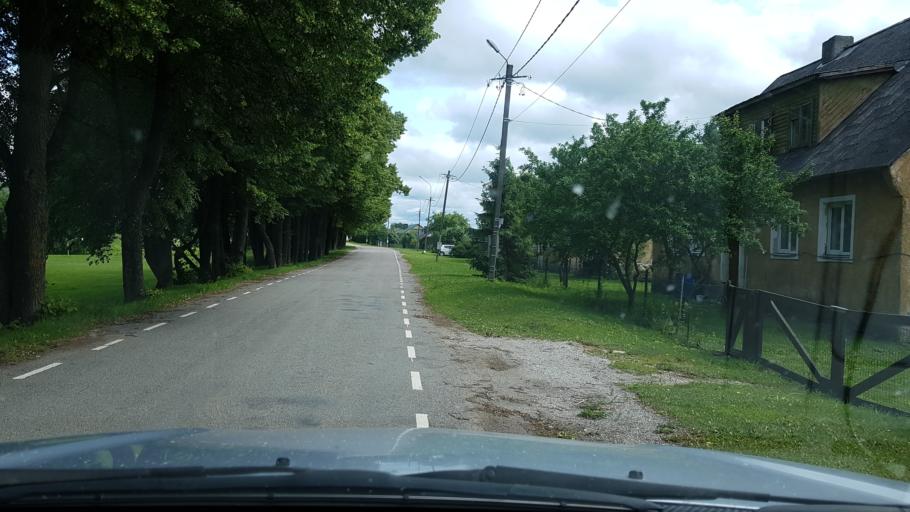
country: EE
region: Ida-Virumaa
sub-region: Sillamaee linn
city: Sillamae
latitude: 59.3733
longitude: 27.8686
